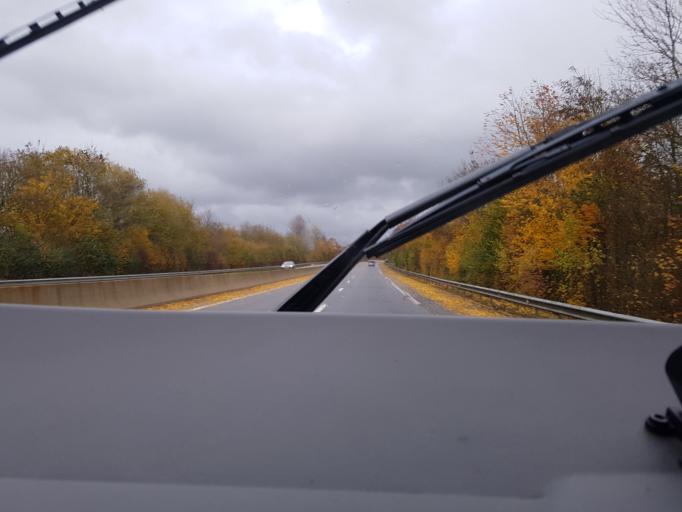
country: FR
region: Nord-Pas-de-Calais
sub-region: Departement du Pas-de-Calais
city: Saint-Pol-sur-Ternoise
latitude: 50.3682
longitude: 2.3543
